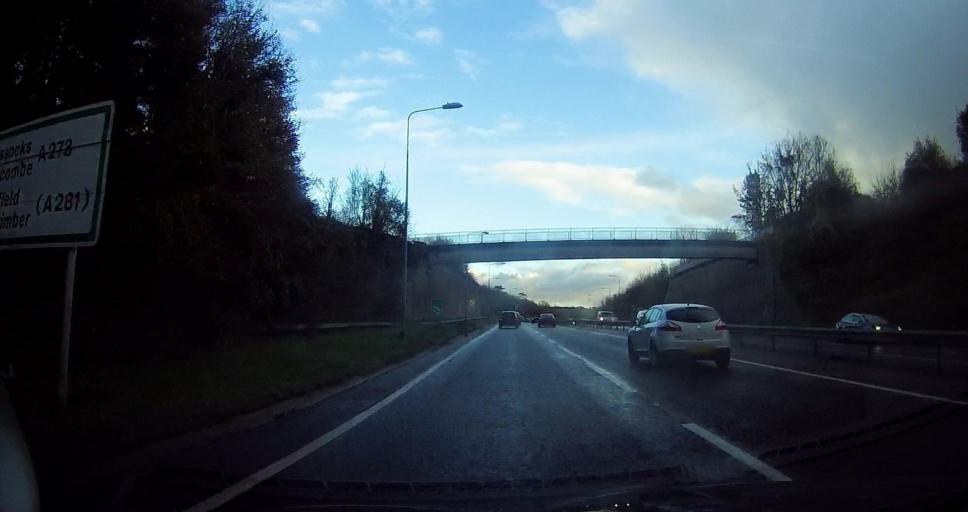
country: GB
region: England
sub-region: West Sussex
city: Hassocks
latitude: 50.9009
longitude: -0.1751
